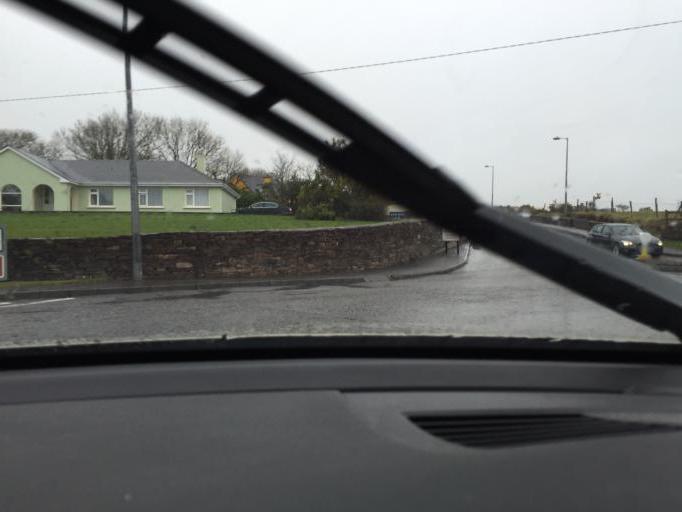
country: IE
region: Munster
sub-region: Ciarrai
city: Dingle
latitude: 52.1422
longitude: -10.2876
